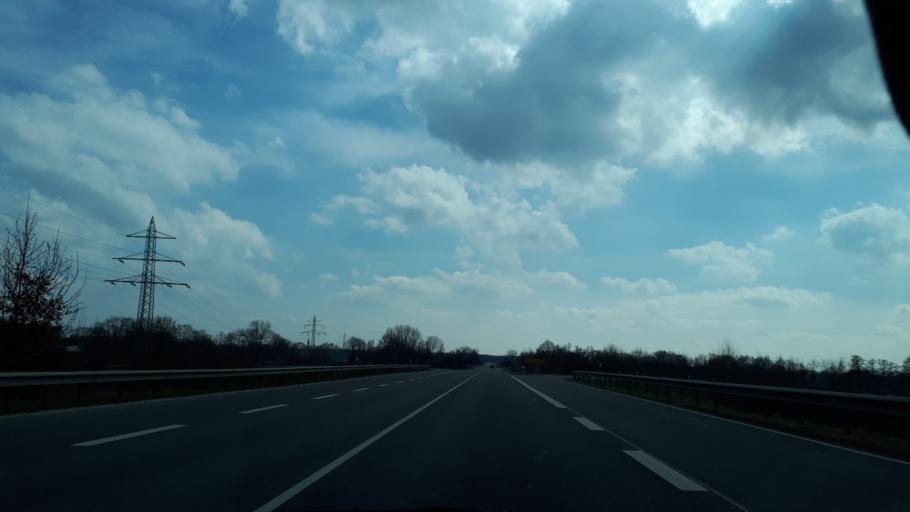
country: DE
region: Lower Saxony
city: Vechta
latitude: 52.7196
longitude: 8.2571
